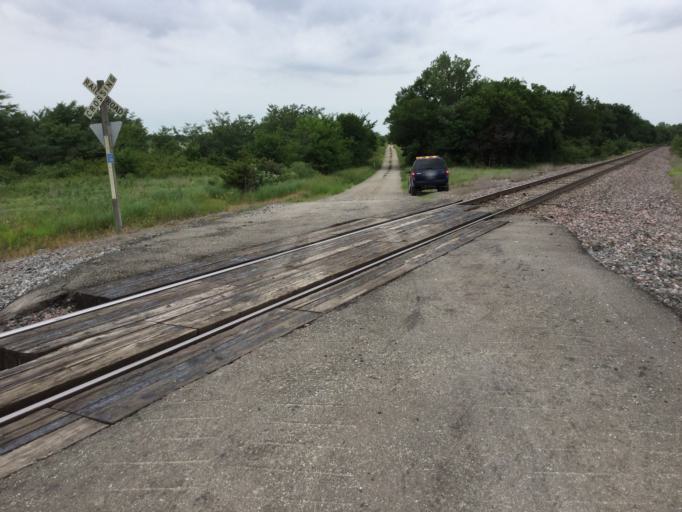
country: US
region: Kansas
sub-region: Anderson County
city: Garnett
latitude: 38.1980
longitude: -95.0399
